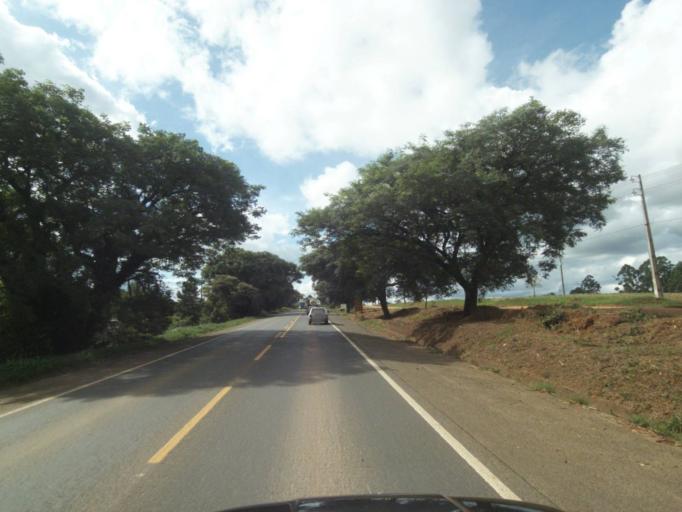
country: BR
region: Parana
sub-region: Telemaco Borba
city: Telemaco Borba
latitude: -24.3506
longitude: -50.6605
